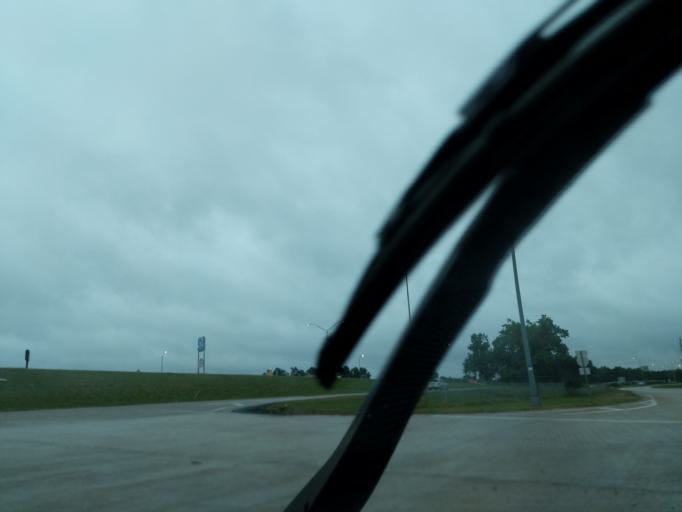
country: US
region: Louisiana
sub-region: Bossier Parish
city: Bossier City
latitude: 32.5282
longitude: -93.6725
